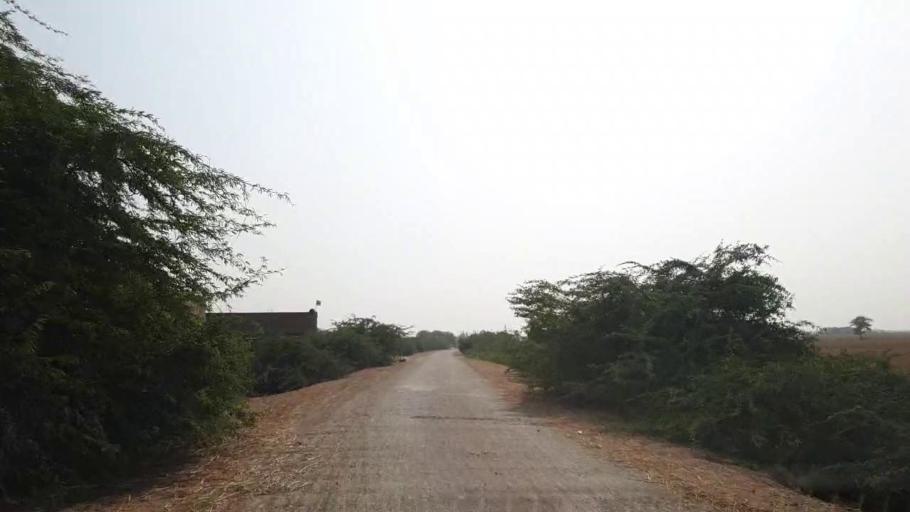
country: PK
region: Sindh
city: Matli
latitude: 25.0029
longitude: 68.5732
